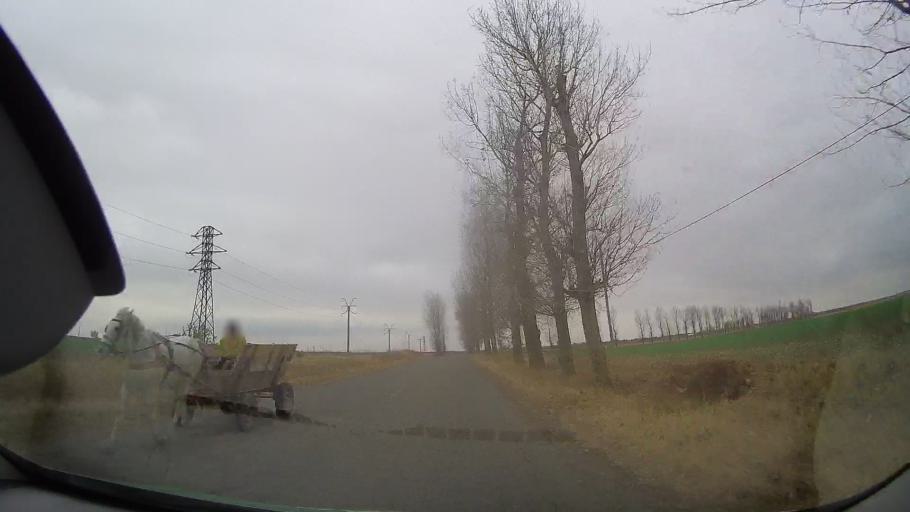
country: RO
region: Buzau
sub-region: Comuna Rusetu
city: Rusetu
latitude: 44.9438
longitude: 27.2347
